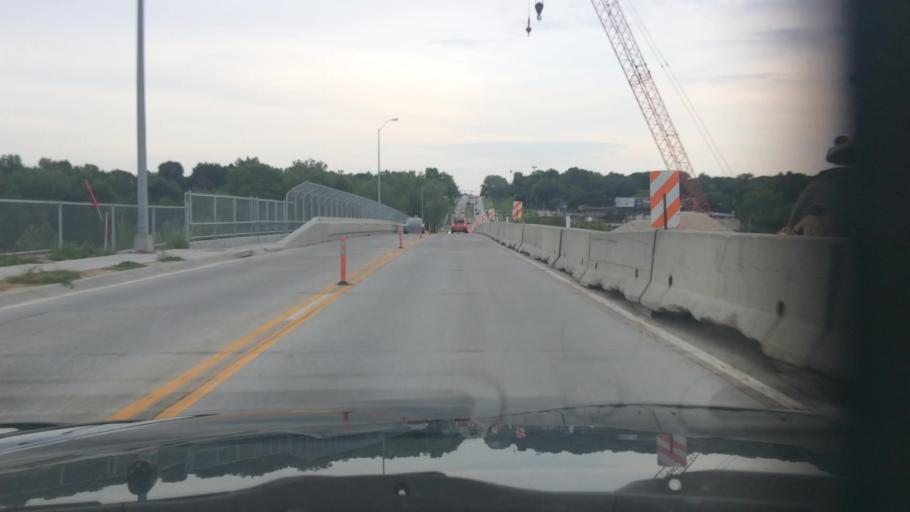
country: US
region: Nebraska
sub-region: Douglas County
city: Ralston
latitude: 41.1993
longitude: -96.0430
